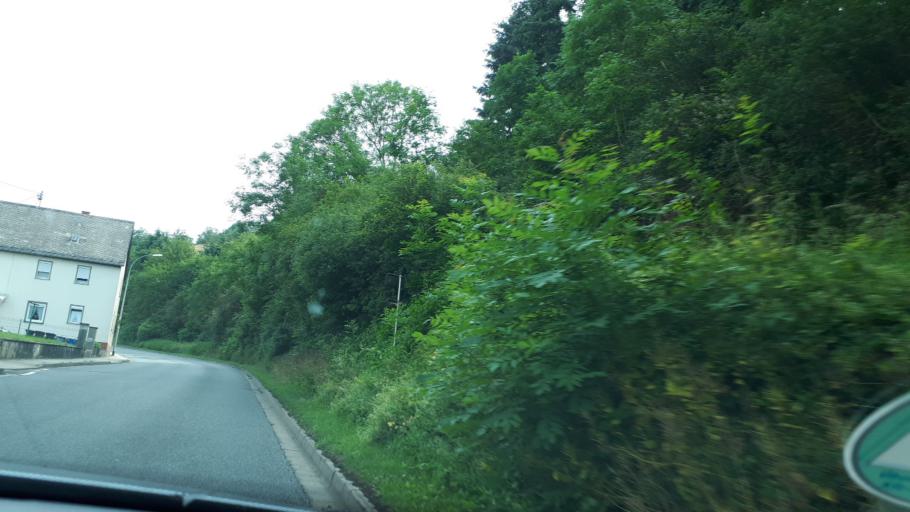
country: DE
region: Rheinland-Pfalz
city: Trimbs
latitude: 50.3257
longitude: 7.3016
